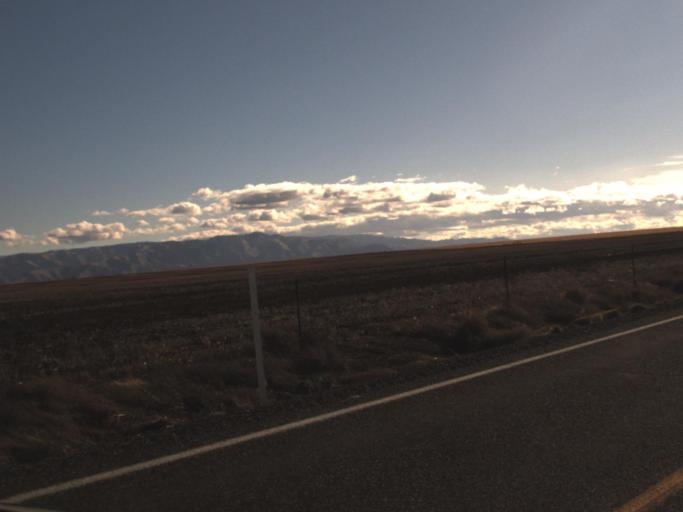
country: US
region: Washington
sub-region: Asotin County
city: Asotin
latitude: 46.2017
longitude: -117.0694
